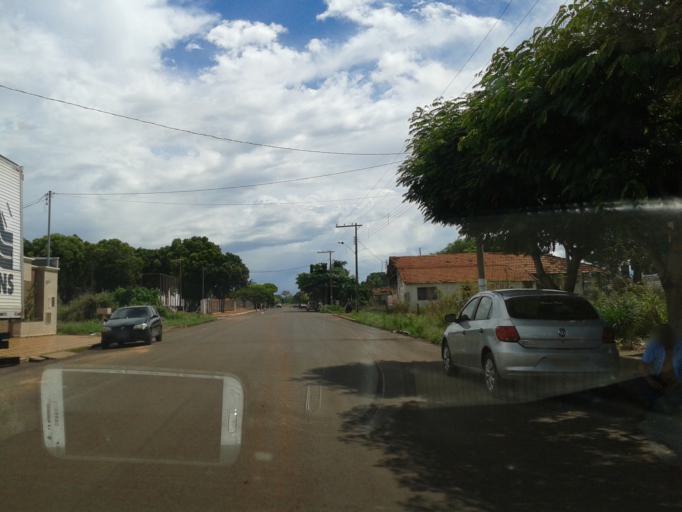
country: BR
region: Minas Gerais
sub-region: Santa Vitoria
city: Santa Vitoria
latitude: -18.8491
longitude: -50.1286
